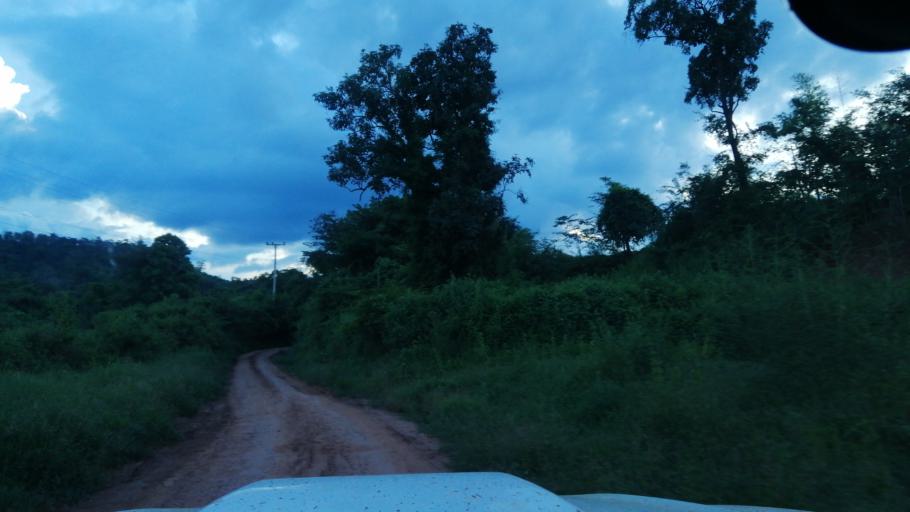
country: TH
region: Uttaradit
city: Ban Khok
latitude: 17.8765
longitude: 101.0776
